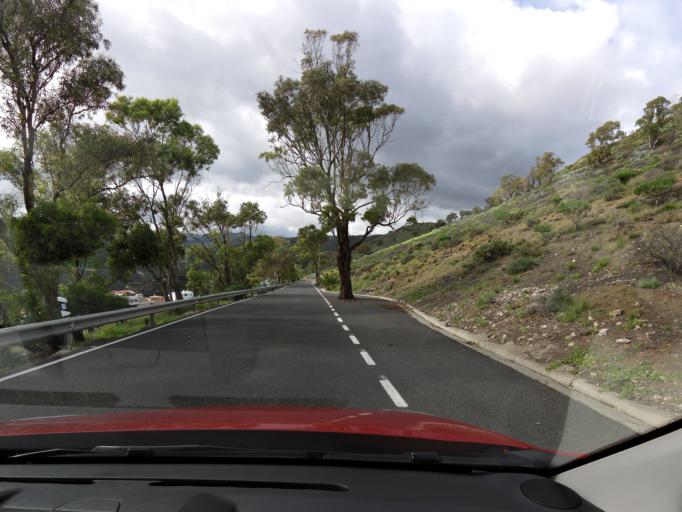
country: ES
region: Canary Islands
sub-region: Provincia de Las Palmas
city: Telde
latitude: 28.0120
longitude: -15.4377
